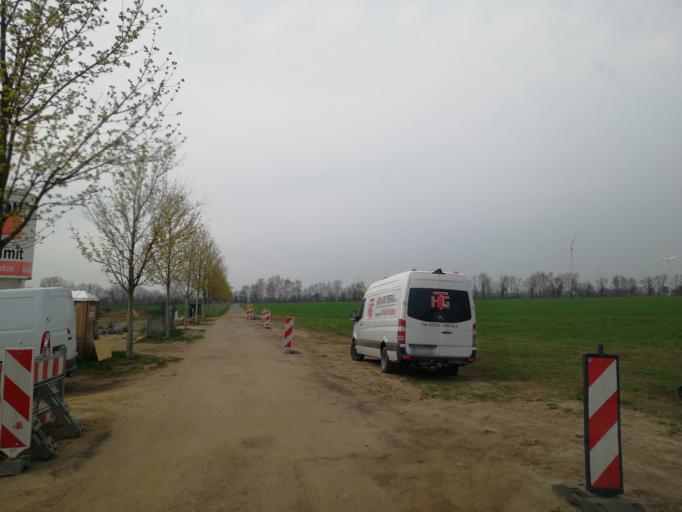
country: DE
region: Brandenburg
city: Elsterwerda
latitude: 51.4297
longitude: 13.4885
